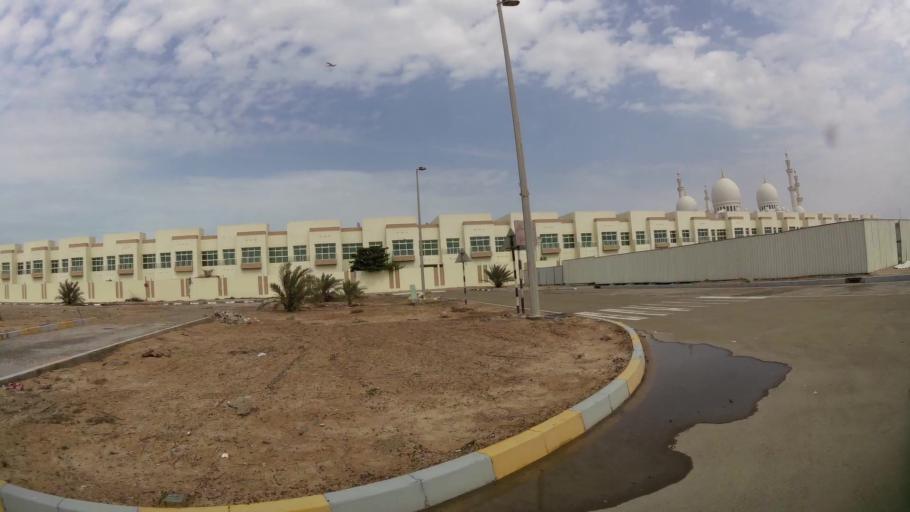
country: AE
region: Abu Dhabi
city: Abu Dhabi
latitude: 24.4106
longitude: 54.4694
